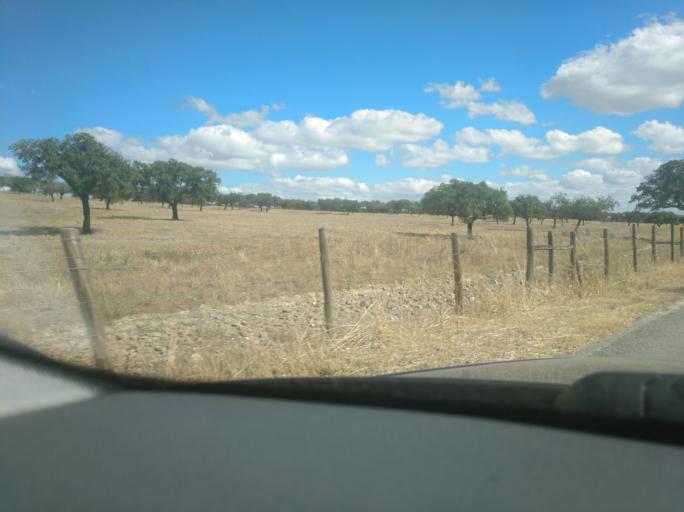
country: ES
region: Extremadura
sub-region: Provincia de Badajoz
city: La Codosera
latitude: 39.1389
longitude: -7.1567
